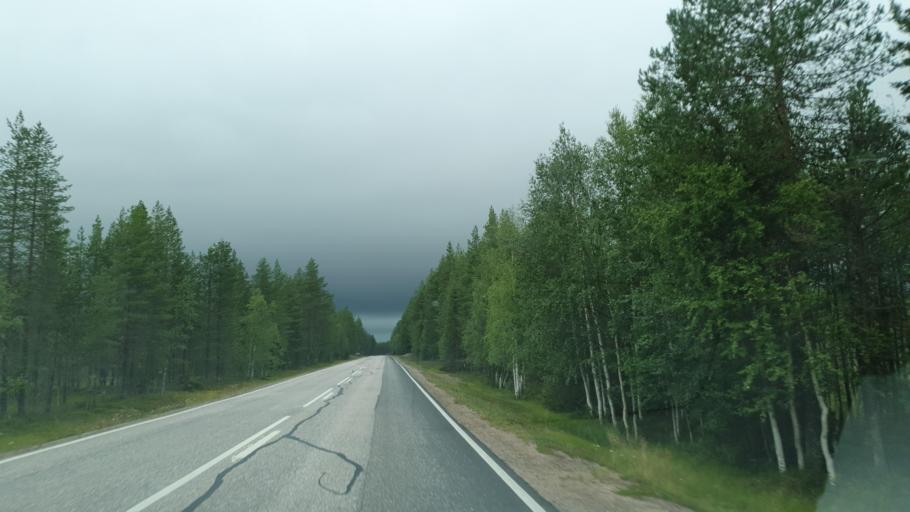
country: FI
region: Lapland
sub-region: Itae-Lappi
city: Posio
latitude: 66.5124
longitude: 28.3179
